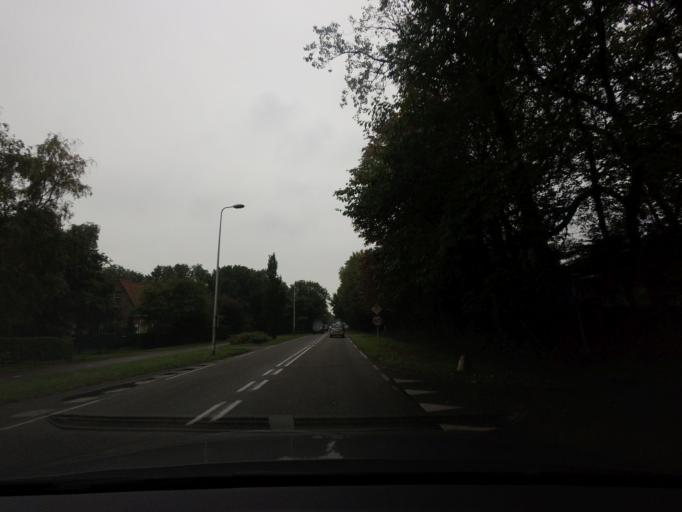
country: NL
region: South Holland
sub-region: Gemeente Noordwijk
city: Noordwijk-Binnen
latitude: 52.2439
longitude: 4.4645
